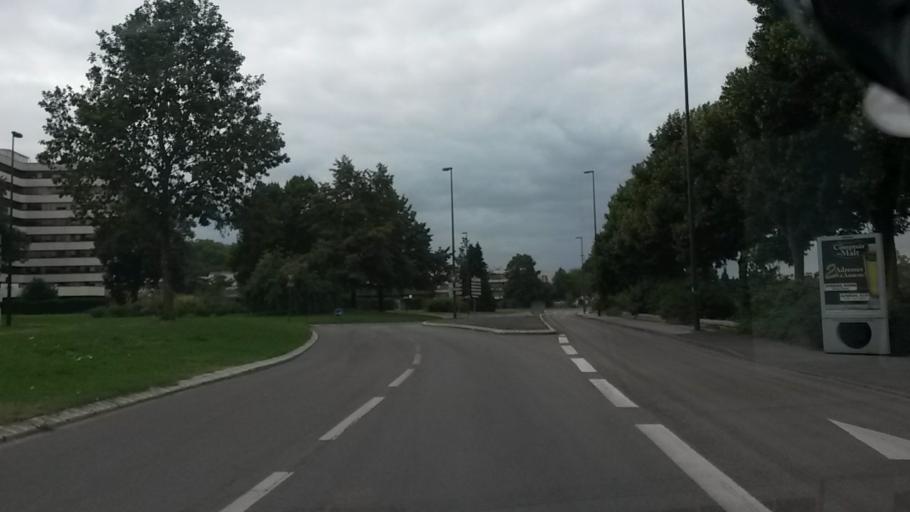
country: FR
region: Picardie
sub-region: Departement de la Somme
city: Amiens
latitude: 49.8987
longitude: 2.2917
